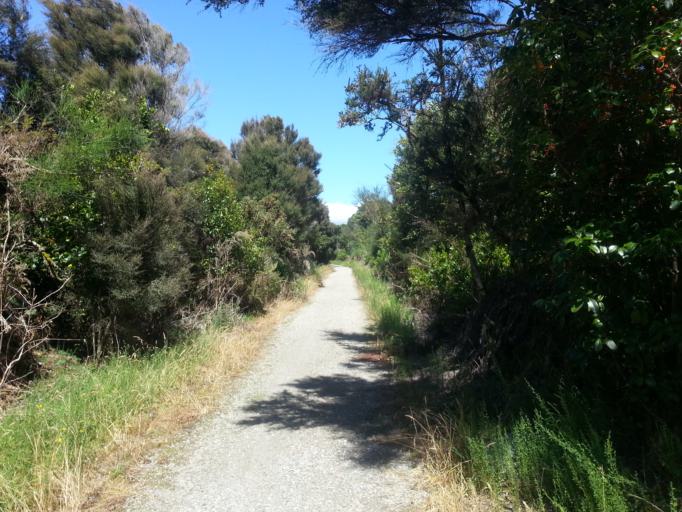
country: NZ
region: West Coast
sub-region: Grey District
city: Greymouth
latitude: -42.6385
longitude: 171.1877
